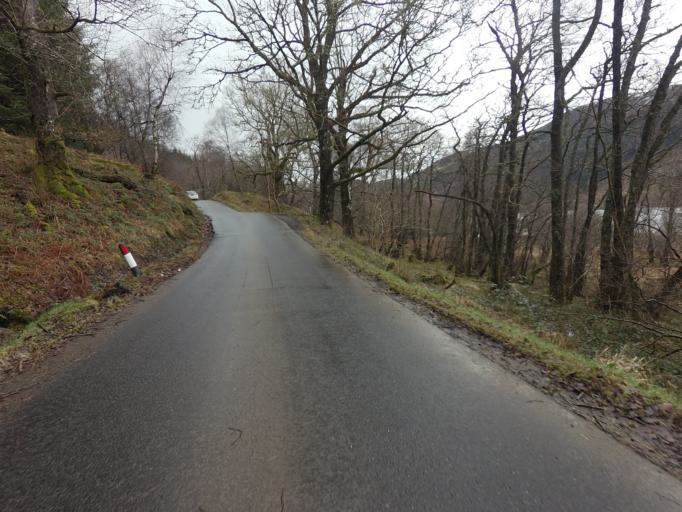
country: GB
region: Scotland
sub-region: West Dunbartonshire
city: Balloch
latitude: 56.2175
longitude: -4.5452
